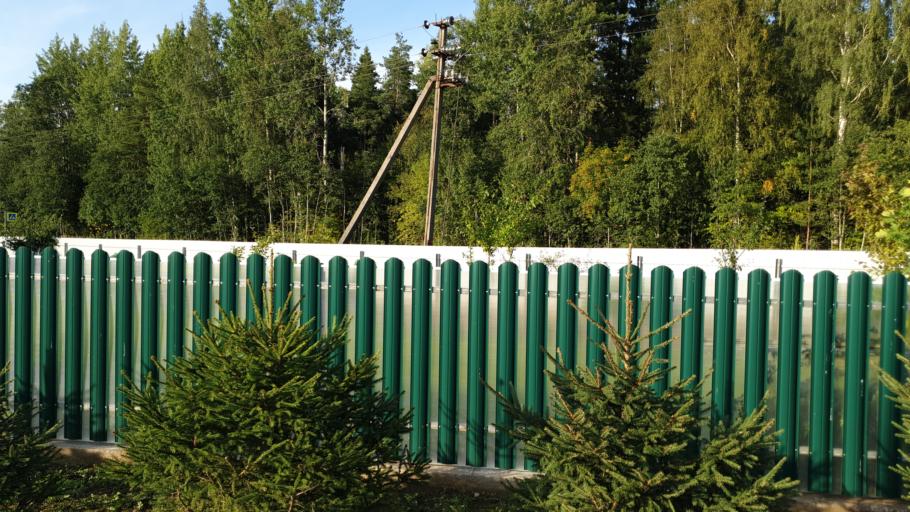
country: RU
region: Leningrad
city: Ivangorod
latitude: 59.4250
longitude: 28.3313
